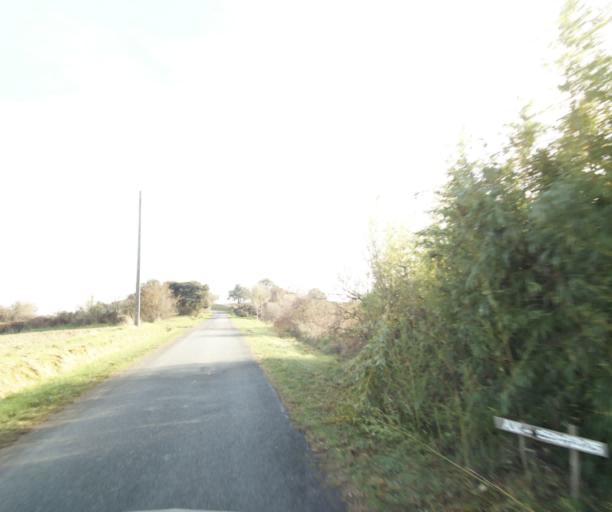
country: FR
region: Midi-Pyrenees
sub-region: Departement de la Haute-Garonne
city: Villemur-sur-Tarn
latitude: 43.8543
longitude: 1.5199
